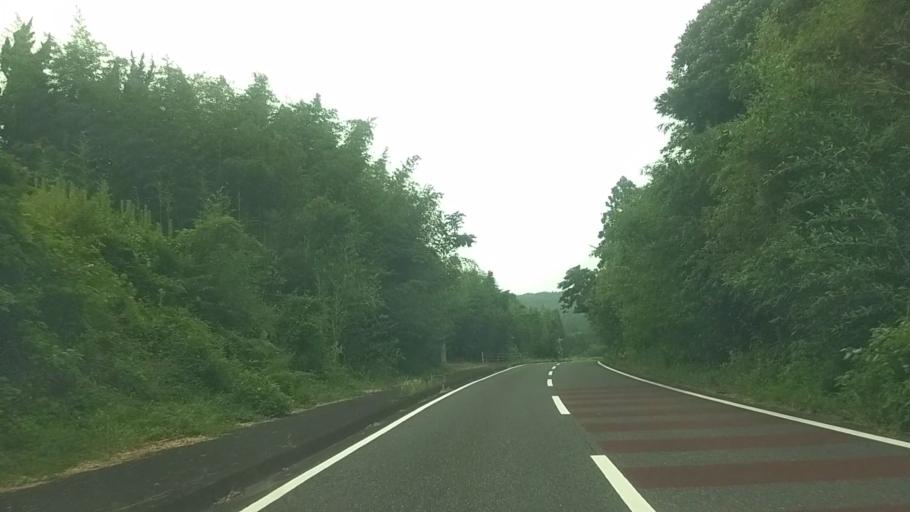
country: JP
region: Chiba
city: Kawaguchi
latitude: 35.2216
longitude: 140.0217
